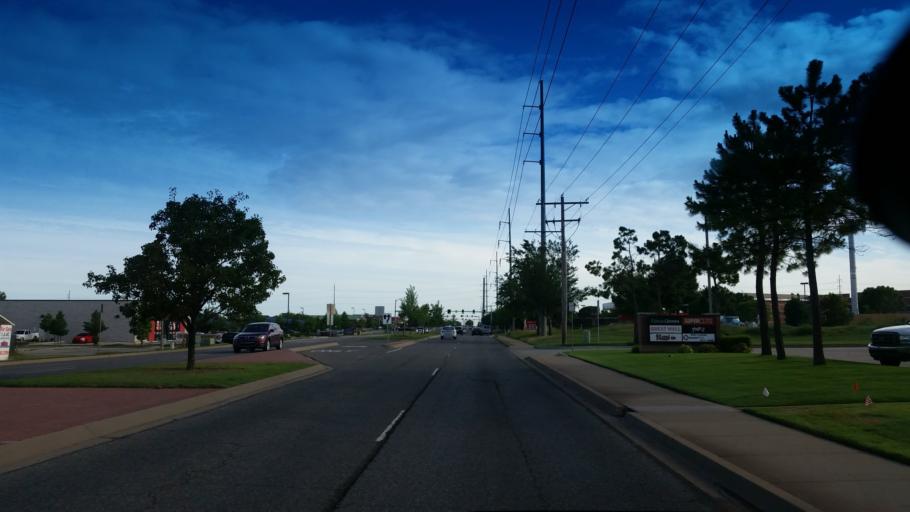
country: US
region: Oklahoma
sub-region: Oklahoma County
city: Edmond
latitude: 35.6636
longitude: -97.5140
